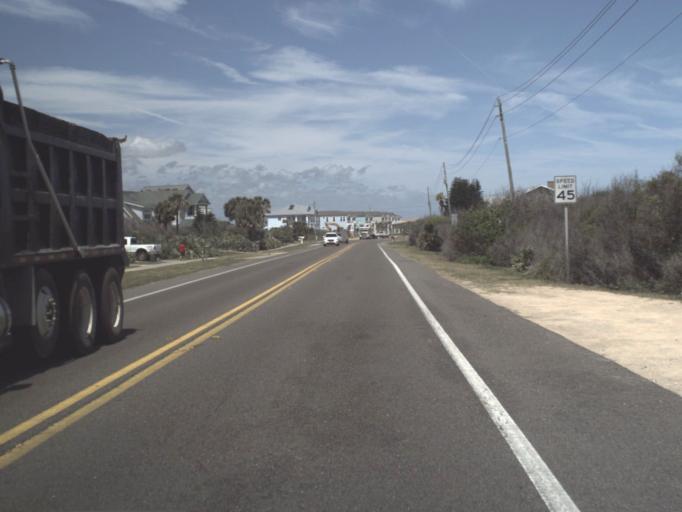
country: US
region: Florida
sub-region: Flagler County
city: Flagler Beach
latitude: 29.5135
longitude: -81.1434
